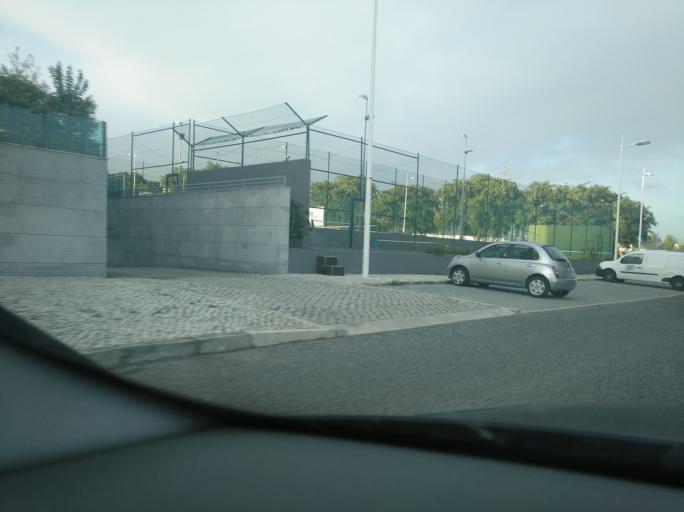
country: PT
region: Lisbon
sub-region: Odivelas
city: Olival do Basto
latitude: 38.7799
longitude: -9.1714
